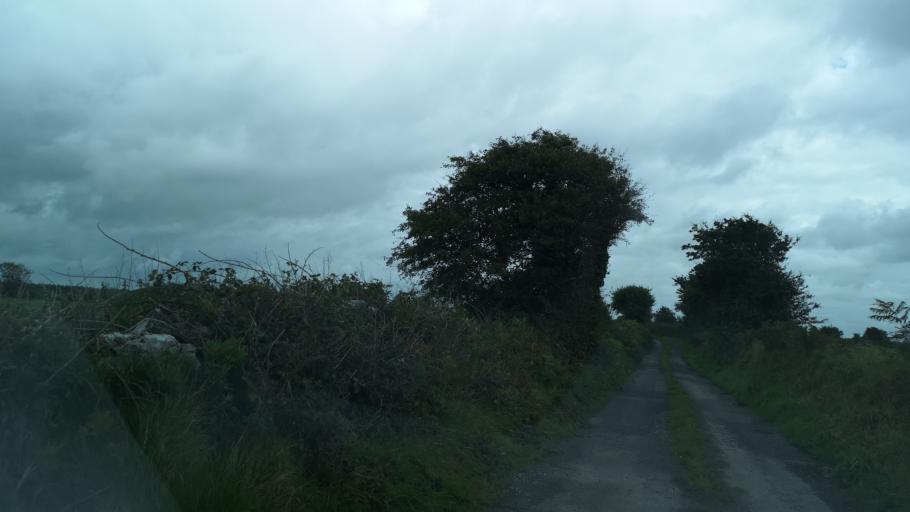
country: IE
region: Connaught
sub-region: County Galway
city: Athenry
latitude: 53.2846
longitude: -8.7135
